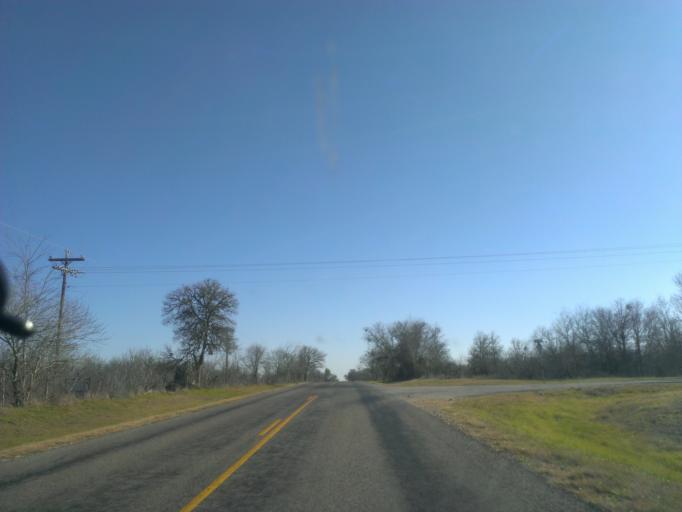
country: US
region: Texas
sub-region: Bastrop County
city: Elgin
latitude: 30.4600
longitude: -97.2699
